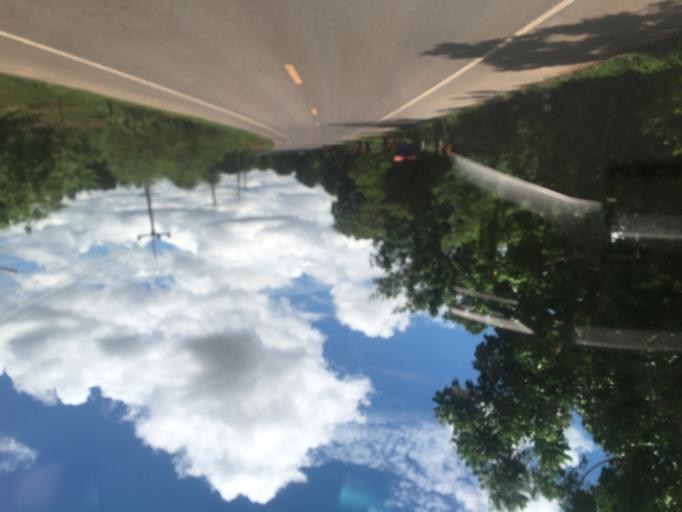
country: TH
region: Changwat Udon Thani
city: Nong Saeng
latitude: 17.1470
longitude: 102.7896
